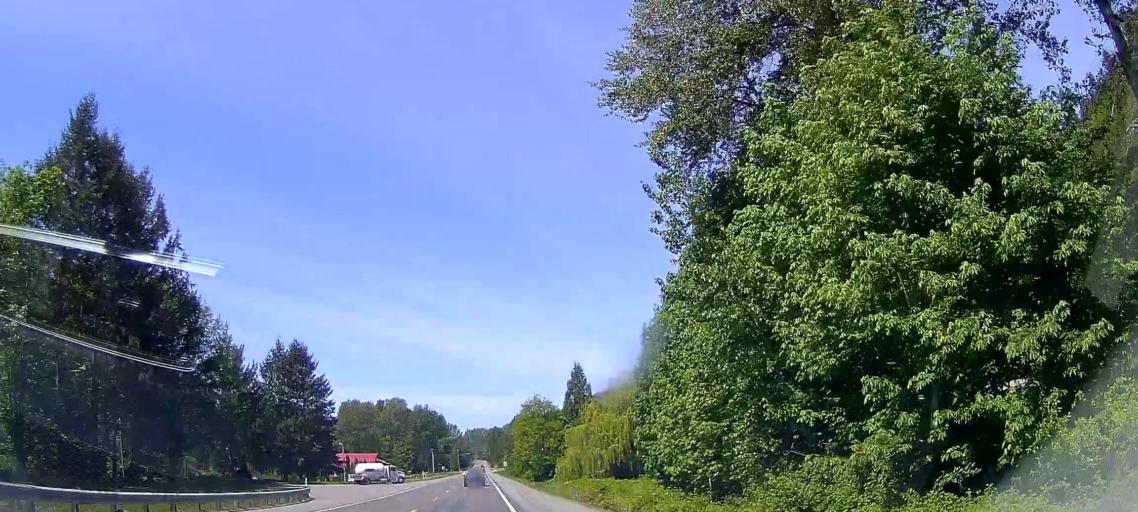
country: US
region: Washington
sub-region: Snohomish County
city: Darrington
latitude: 48.5352
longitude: -121.7342
